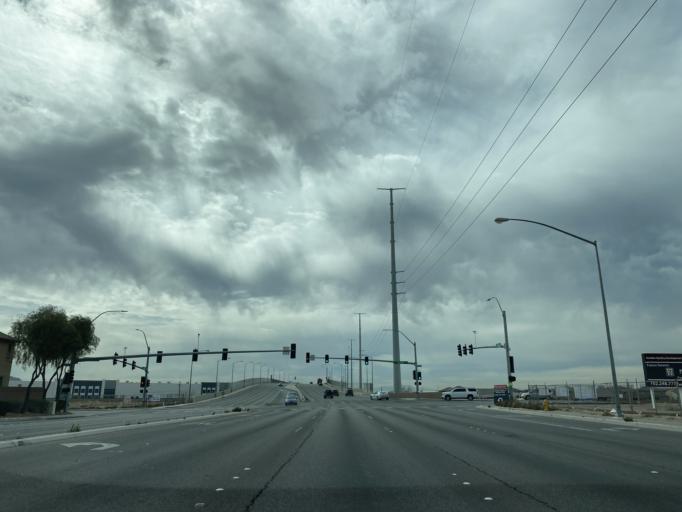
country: US
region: Nevada
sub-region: Clark County
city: Nellis Air Force Base
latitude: 36.2702
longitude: -115.0801
